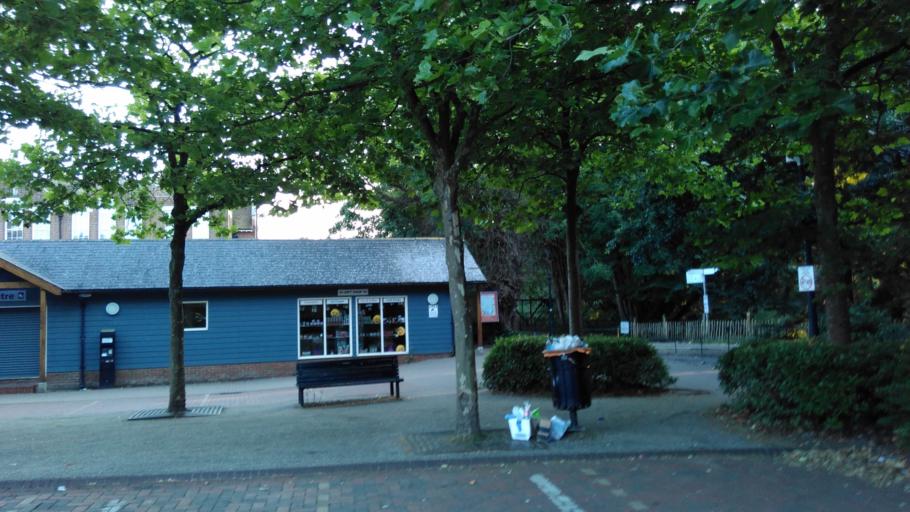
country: GB
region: England
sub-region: Kent
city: Canterbury
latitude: 51.2843
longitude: 1.0833
